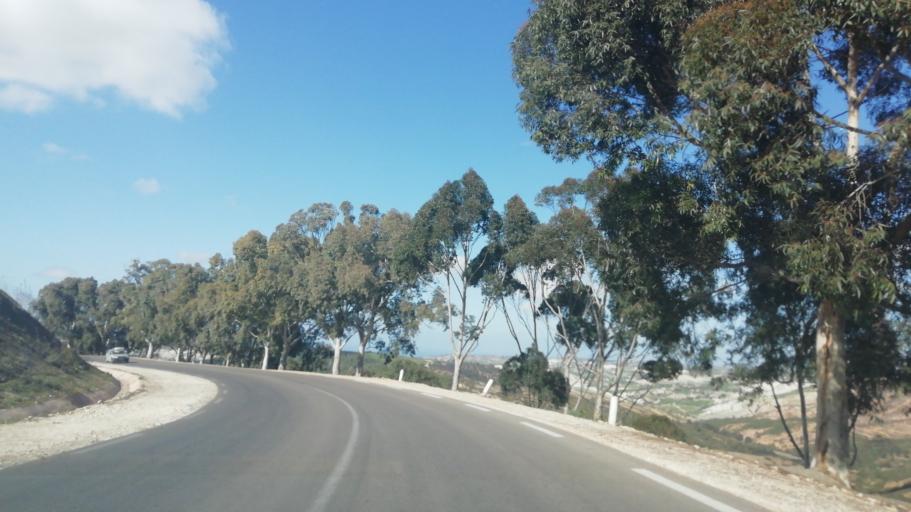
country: DZ
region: Relizane
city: Relizane
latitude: 36.0888
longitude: 0.4744
